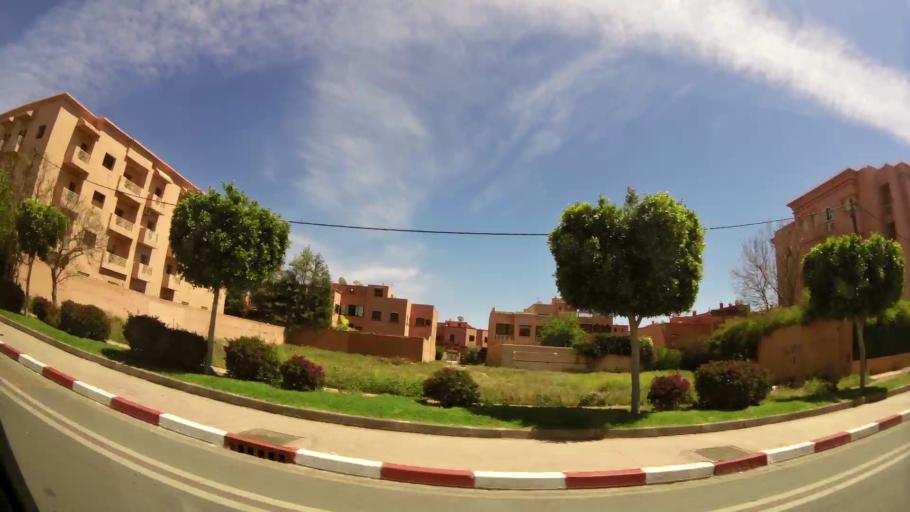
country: MA
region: Marrakech-Tensift-Al Haouz
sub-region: Marrakech
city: Marrakesh
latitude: 31.6711
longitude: -8.0075
